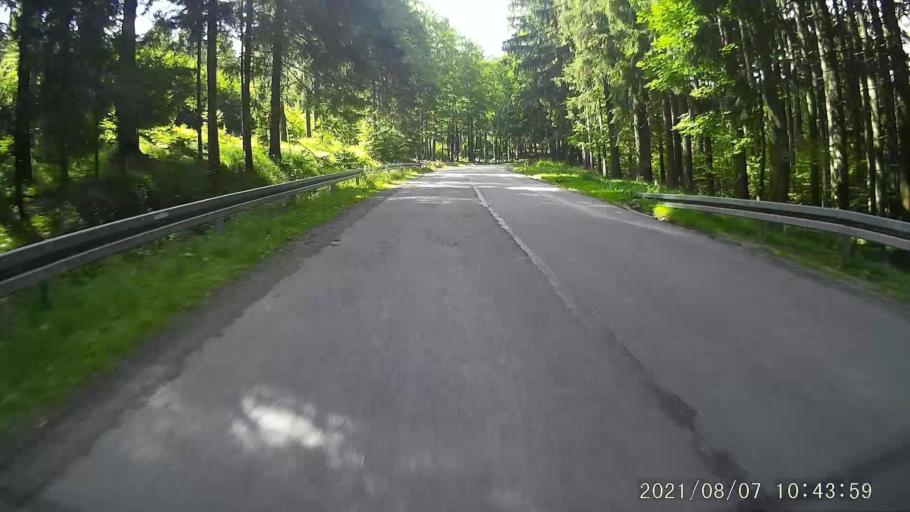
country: PL
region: Lower Silesian Voivodeship
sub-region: Powiat klodzki
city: Duszniki-Zdroj
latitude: 50.3283
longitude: 16.4030
